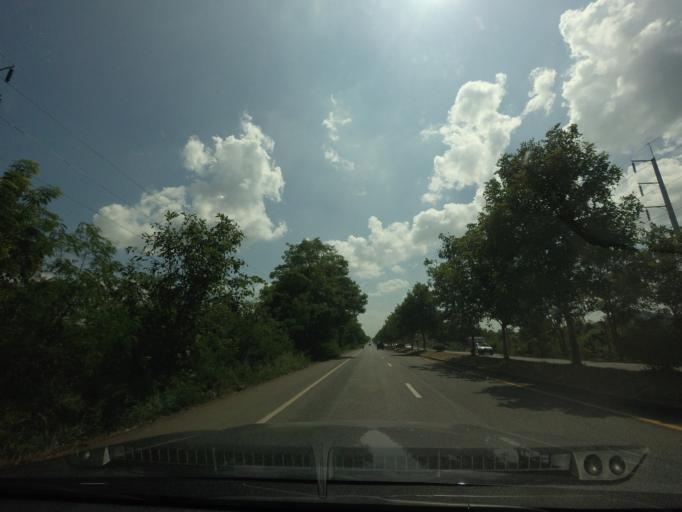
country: TH
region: Phetchabun
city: Nong Phai
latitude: 16.0283
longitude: 101.0757
